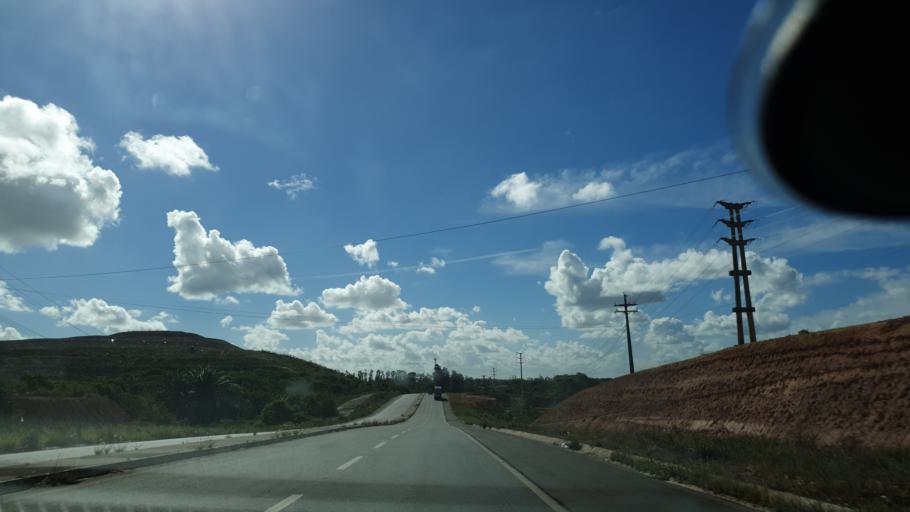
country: BR
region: Bahia
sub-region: Camacari
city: Camacari
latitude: -12.6853
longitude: -38.2552
